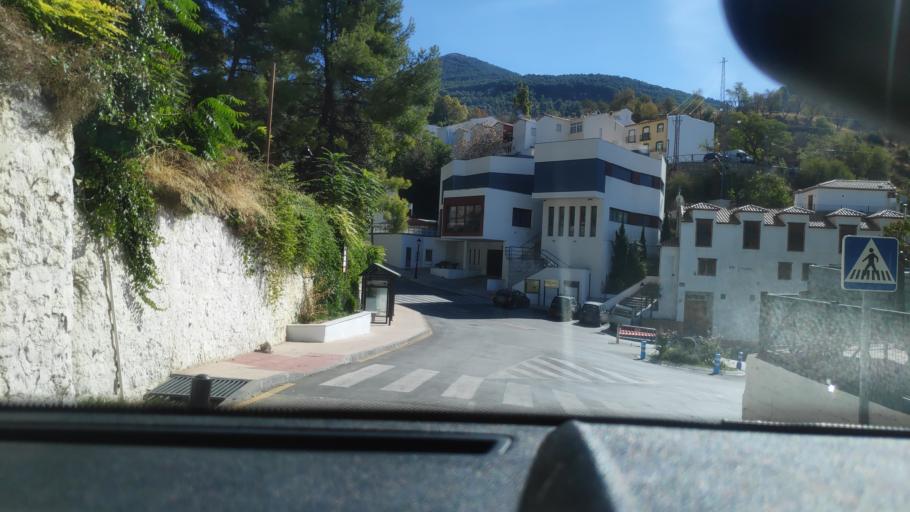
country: ES
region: Andalusia
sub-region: Provincia de Jaen
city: Torres
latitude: 37.7842
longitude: -3.5050
